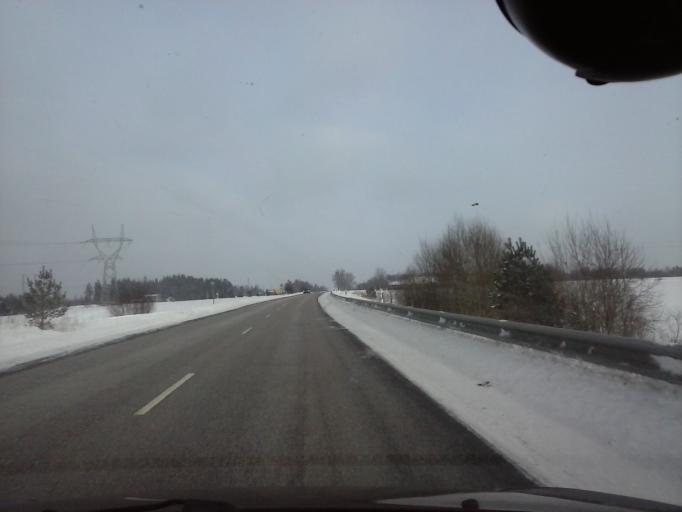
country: EE
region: Paernumaa
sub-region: Saarde vald
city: Kilingi-Nomme
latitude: 58.1642
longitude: 25.0142
